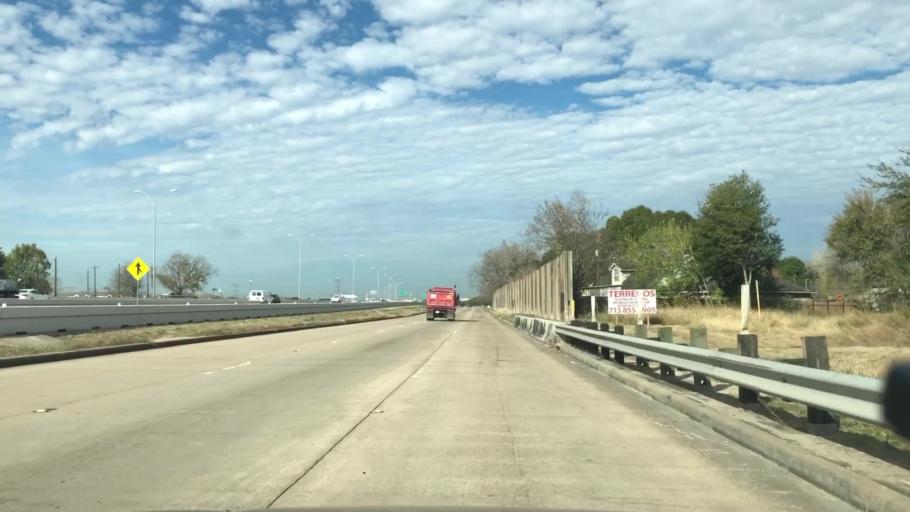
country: US
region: Texas
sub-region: Fort Bend County
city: Missouri City
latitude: 29.6166
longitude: -95.4987
